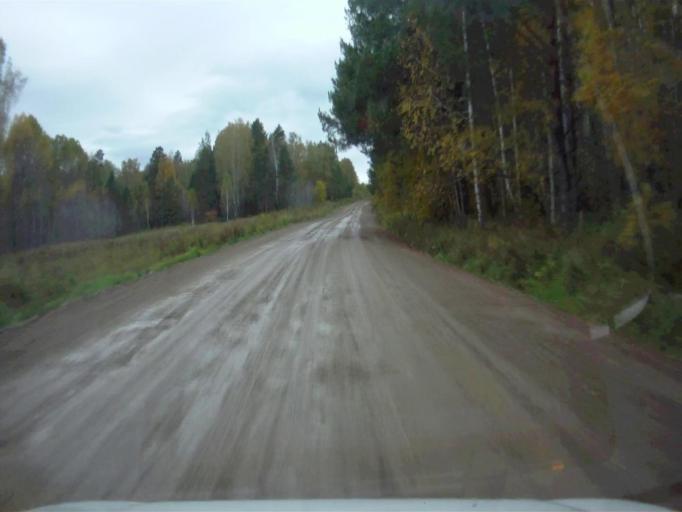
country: RU
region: Chelyabinsk
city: Nyazepetrovsk
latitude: 56.0966
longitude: 59.3983
